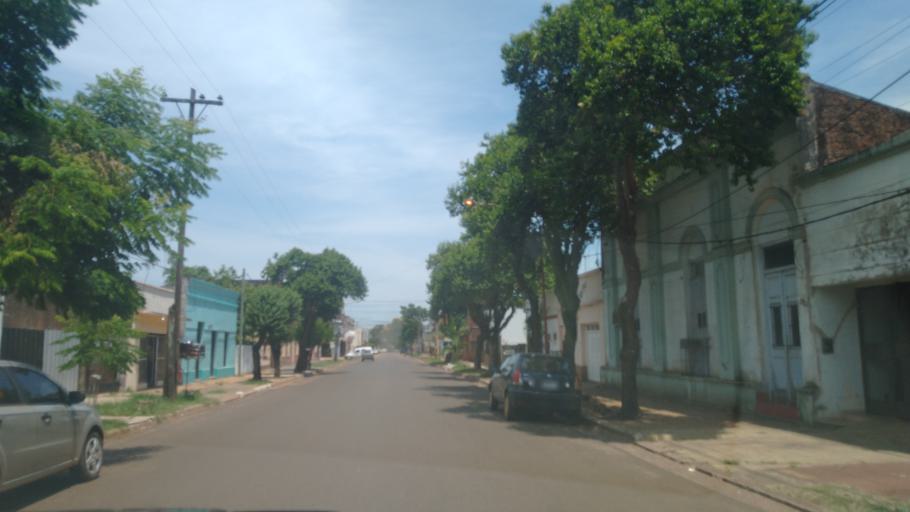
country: AR
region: Corrientes
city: Santo Tome
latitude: -28.5507
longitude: -56.0383
